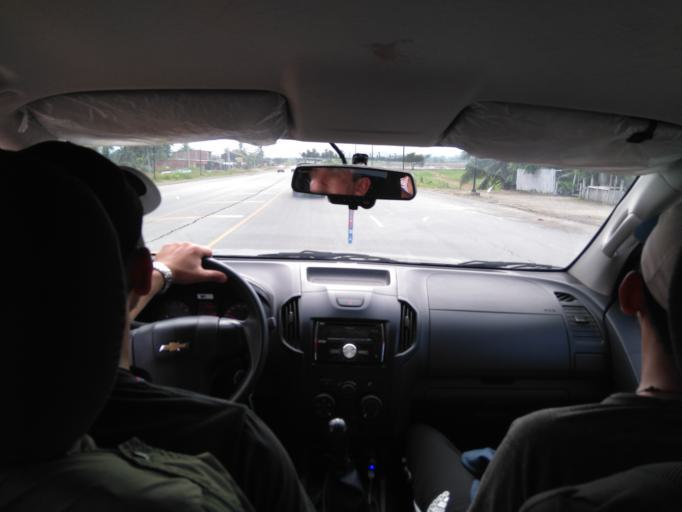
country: EC
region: Manabi
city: Rocafuerte
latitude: -0.9227
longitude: -80.4697
